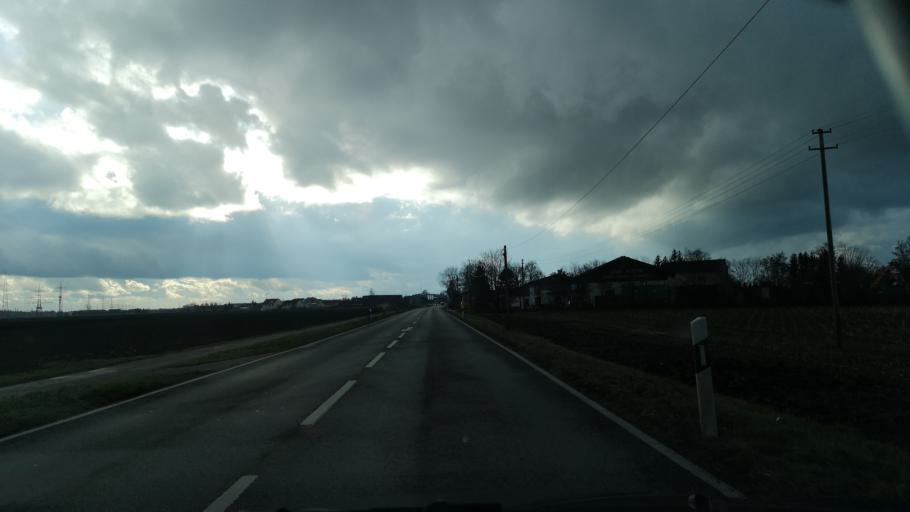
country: DE
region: Bavaria
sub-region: Upper Bavaria
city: Pliening
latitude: 48.1923
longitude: 11.7854
